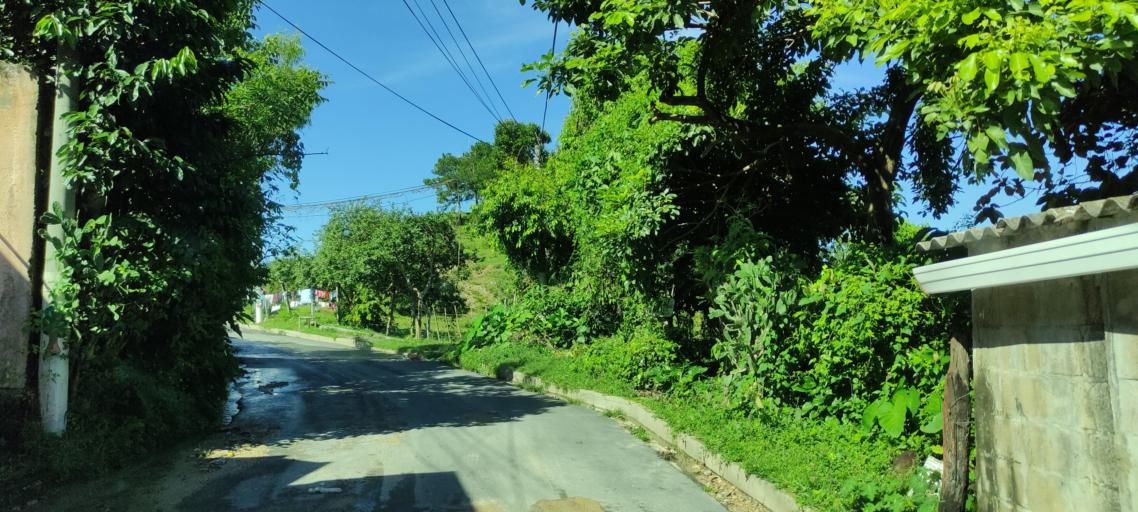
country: HN
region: Ocotepeque
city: Antigua Ocotepeque
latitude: 14.3147
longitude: -89.1747
